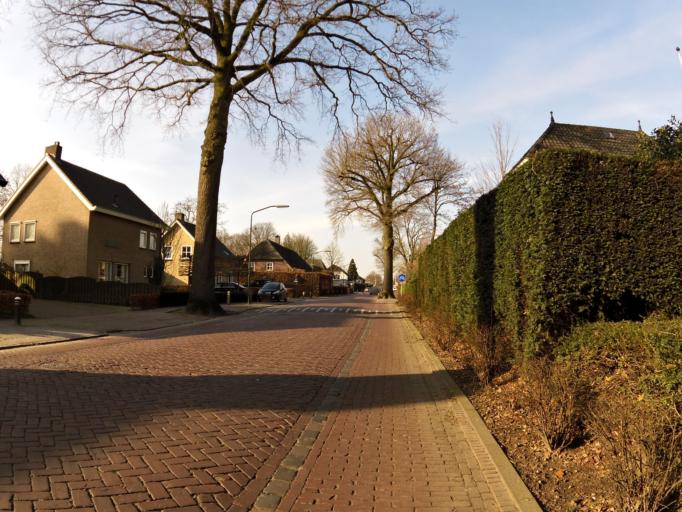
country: NL
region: North Brabant
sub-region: Gemeente Haaren
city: Haaren
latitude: 51.6343
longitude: 5.2341
